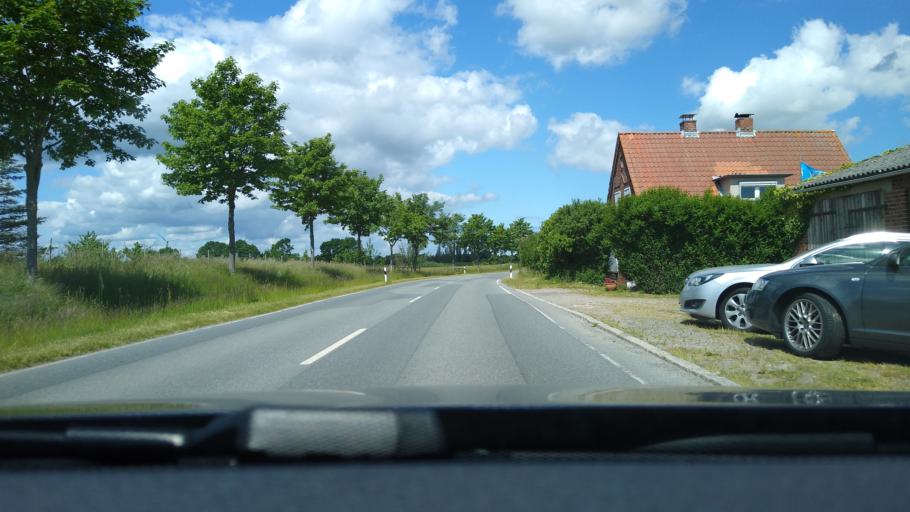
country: DE
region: Schleswig-Holstein
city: Riepsdorf
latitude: 54.2007
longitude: 10.9681
